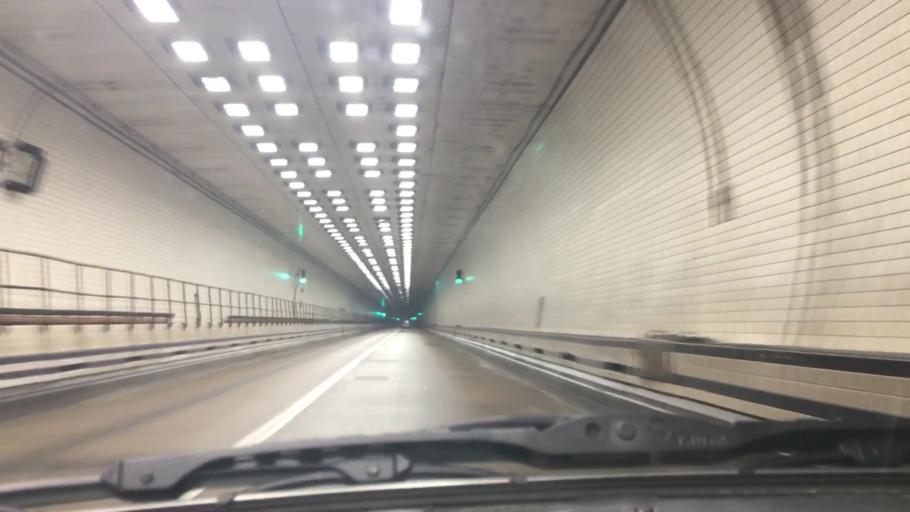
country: US
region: Virginia
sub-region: City of Newport News
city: Newport News
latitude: 36.9592
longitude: -76.4107
